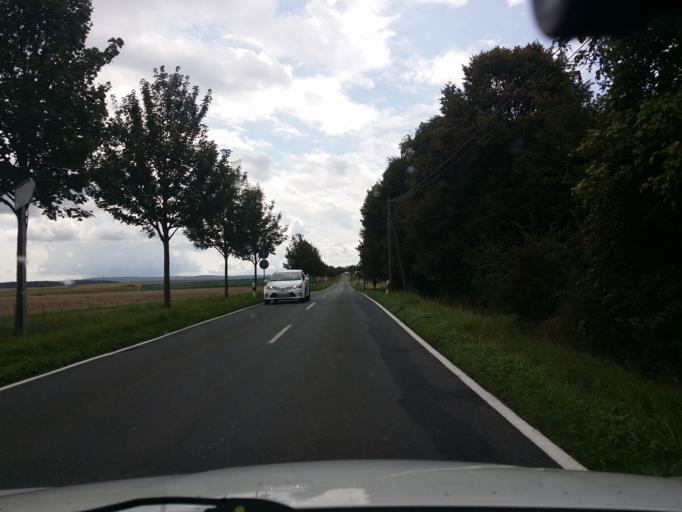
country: DE
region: Hesse
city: Bad Camberg
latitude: 50.2611
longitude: 8.2734
